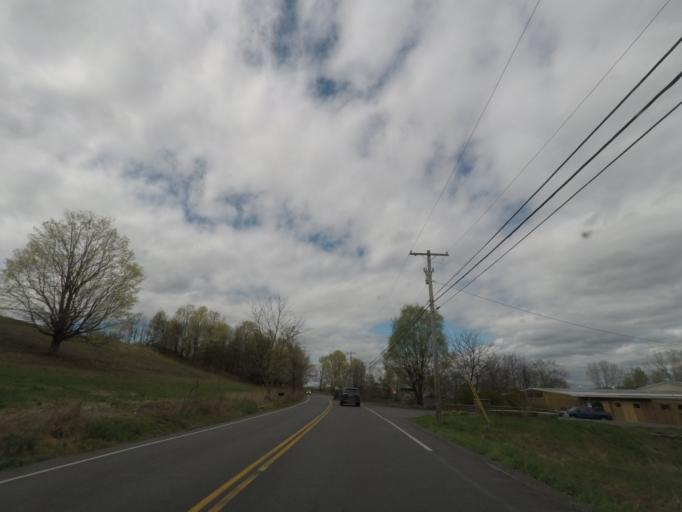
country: US
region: New York
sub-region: Columbia County
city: Valatie
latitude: 42.3811
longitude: -73.6397
